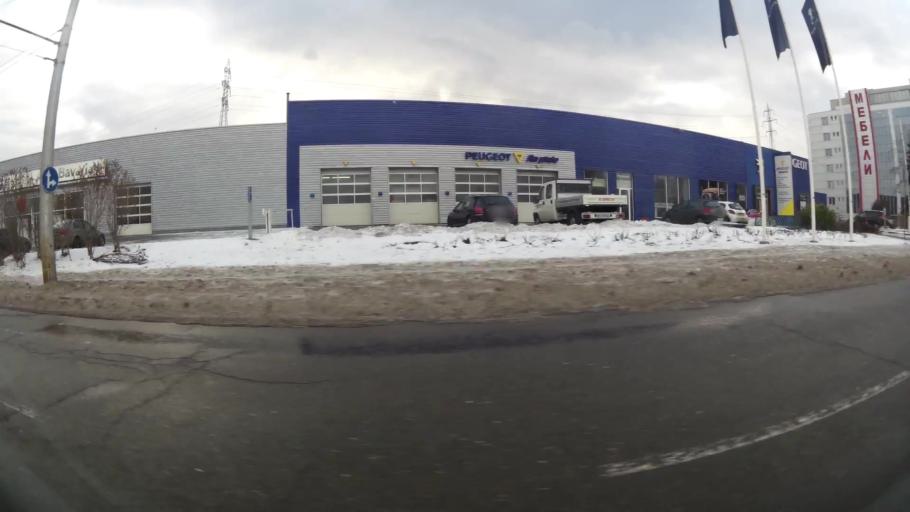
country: BG
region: Sofia-Capital
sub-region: Stolichna Obshtina
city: Sofia
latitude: 42.7122
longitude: 23.2739
